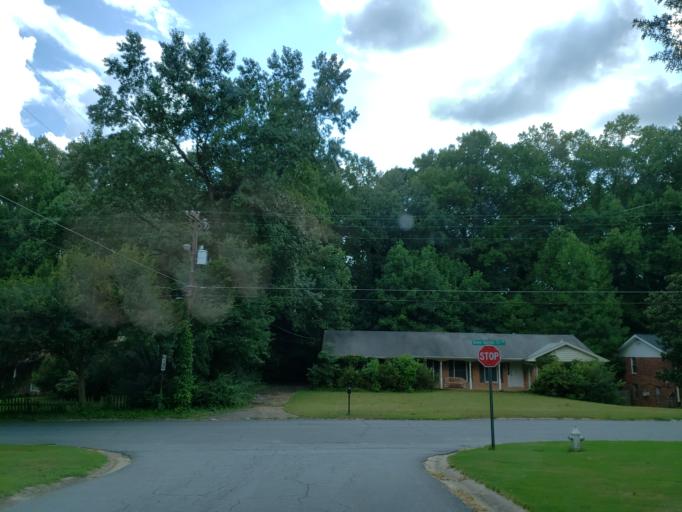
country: US
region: Georgia
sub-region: Fulton County
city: Sandy Springs
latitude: 33.9764
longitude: -84.4321
